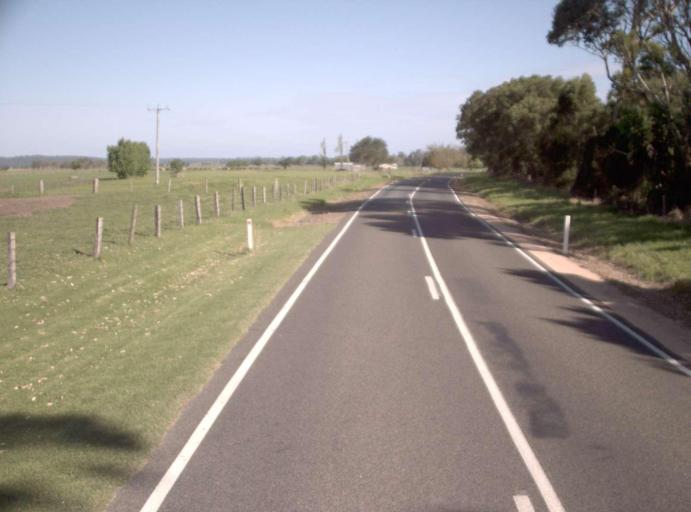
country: AU
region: Victoria
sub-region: East Gippsland
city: Lakes Entrance
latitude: -37.7436
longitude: 148.5140
